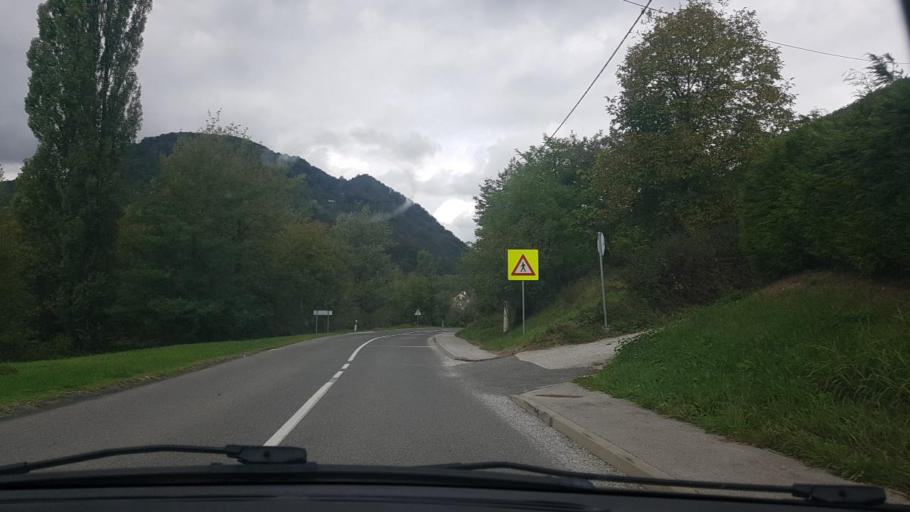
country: SI
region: Bistrica ob Sotli
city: Bistrica ob Sotli
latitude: 46.0477
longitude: 15.7314
